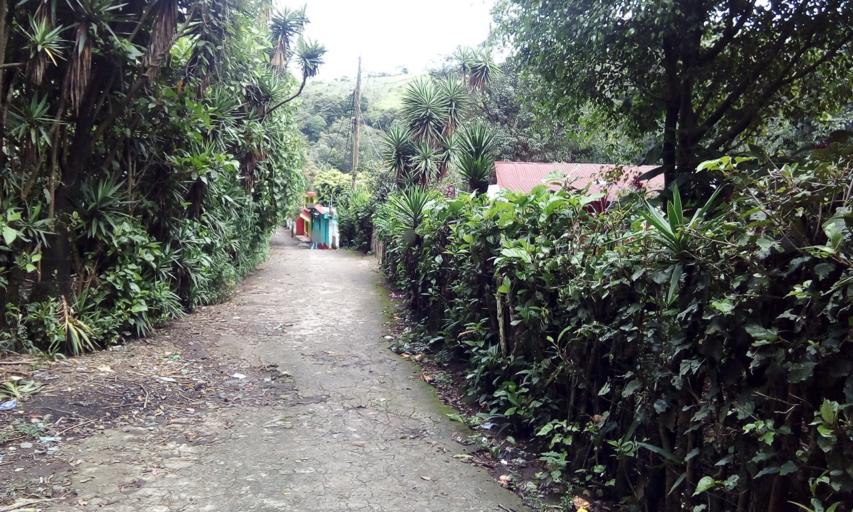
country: GT
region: Escuintla
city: San Vicente Pacaya
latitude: 14.3298
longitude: -90.6038
